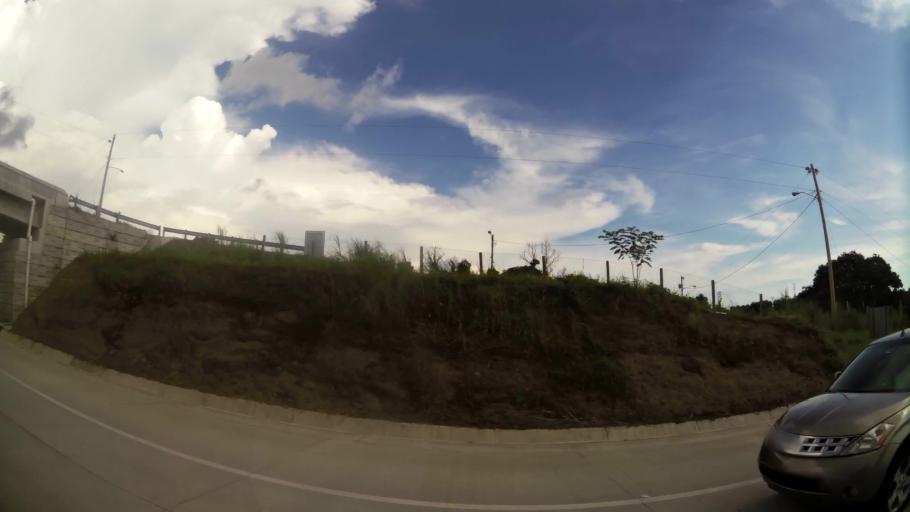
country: PA
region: Panama
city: Tocumen
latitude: 9.0973
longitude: -79.4210
